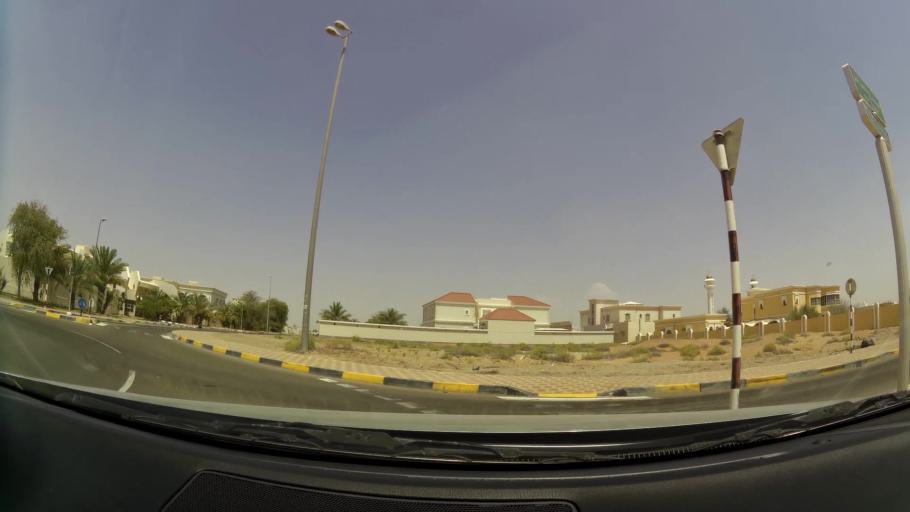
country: OM
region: Al Buraimi
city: Al Buraymi
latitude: 24.2637
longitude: 55.7063
